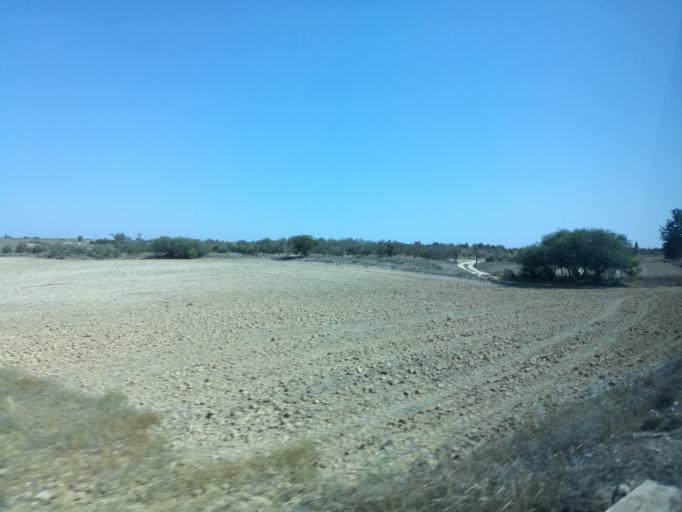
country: CY
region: Ammochostos
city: Acheritou
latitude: 35.0745
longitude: 33.8642
